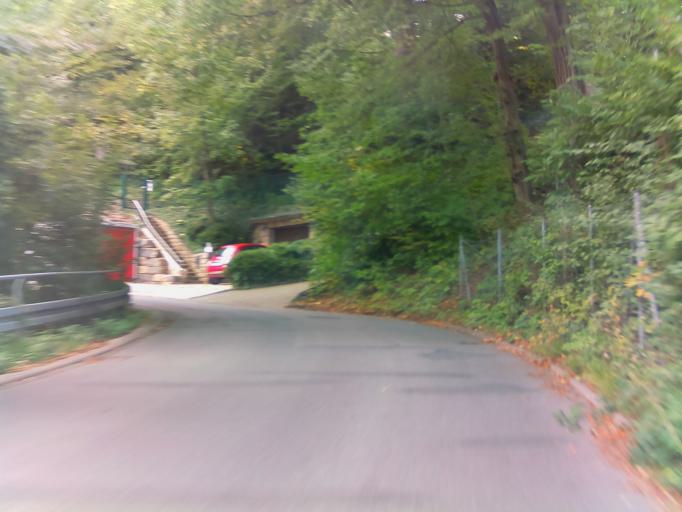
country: DE
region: Baden-Wuerttemberg
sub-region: Karlsruhe Region
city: Schriesheim
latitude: 49.4785
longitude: 8.6753
